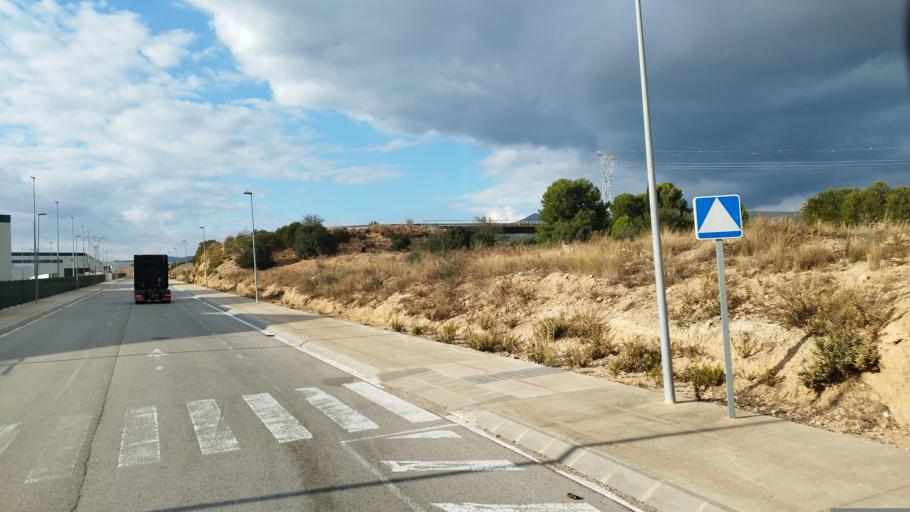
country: ES
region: Catalonia
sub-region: Provincia de Tarragona
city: la Bisbal del Penedes
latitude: 41.2748
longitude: 1.5169
